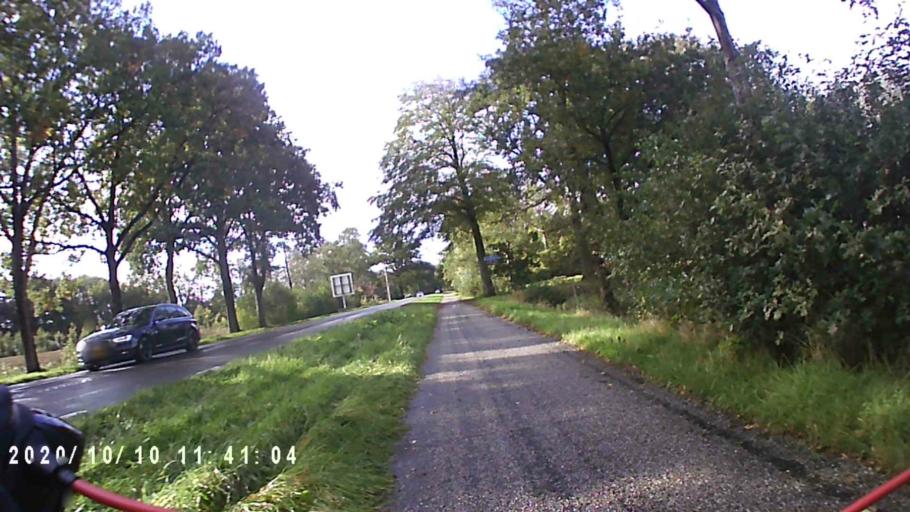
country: NL
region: Friesland
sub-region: Gemeente Smallingerland
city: Drachten
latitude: 53.0656
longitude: 6.1024
